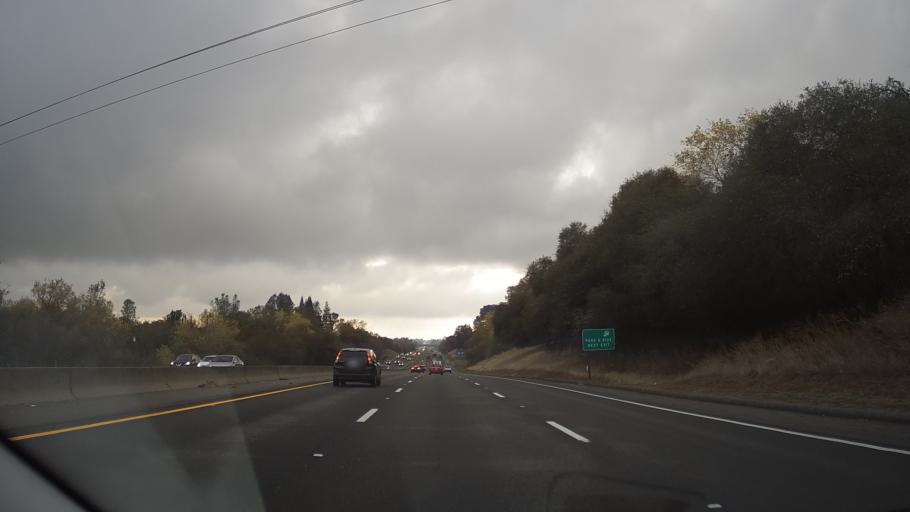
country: US
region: California
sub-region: Placer County
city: Newcastle
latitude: 38.8445
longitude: -121.1560
